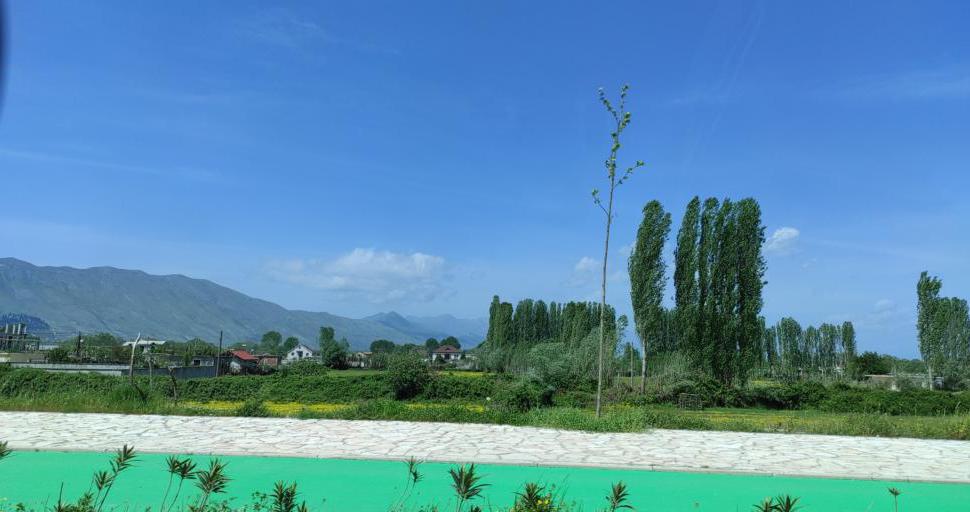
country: AL
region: Shkoder
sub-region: Rrethi i Shkodres
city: Shkoder
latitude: 42.0798
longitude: 19.4922
